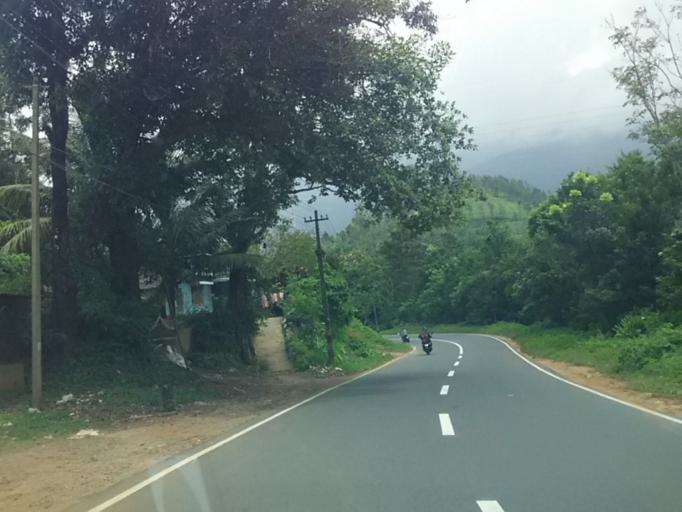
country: IN
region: Kerala
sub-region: Wayanad
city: Kalpetta
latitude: 11.5346
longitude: 76.0321
